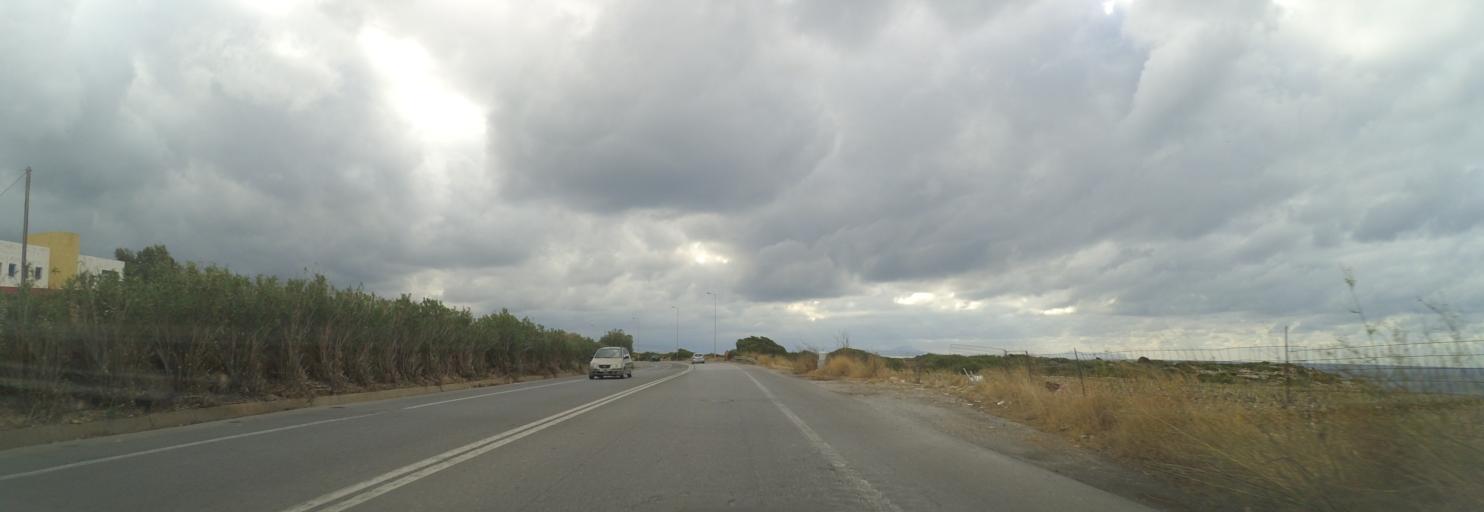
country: GR
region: Crete
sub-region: Nomos Rethymnis
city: Panormos
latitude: 35.3994
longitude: 24.6212
